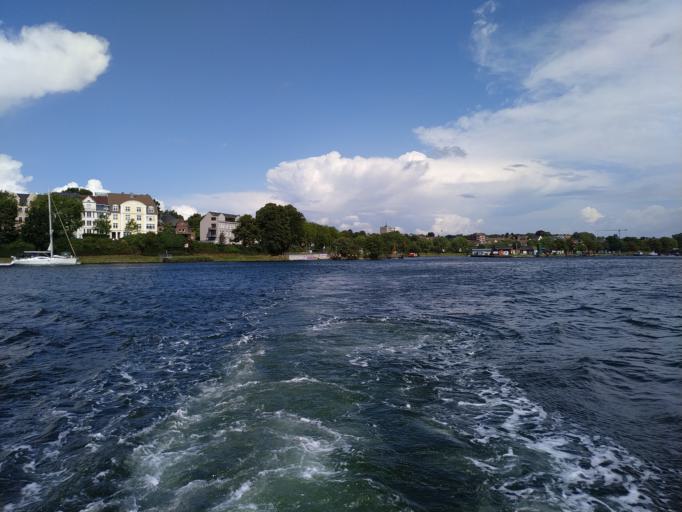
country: DE
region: Schleswig-Holstein
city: Altenholz
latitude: 54.3673
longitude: 10.1322
